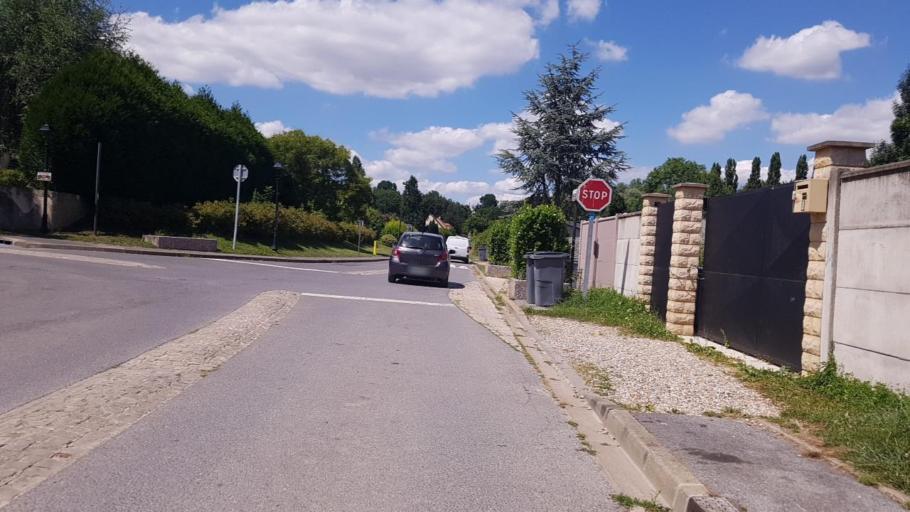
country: FR
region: Ile-de-France
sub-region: Departement de Seine-et-Marne
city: Juilly
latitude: 48.9898
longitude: 2.6692
